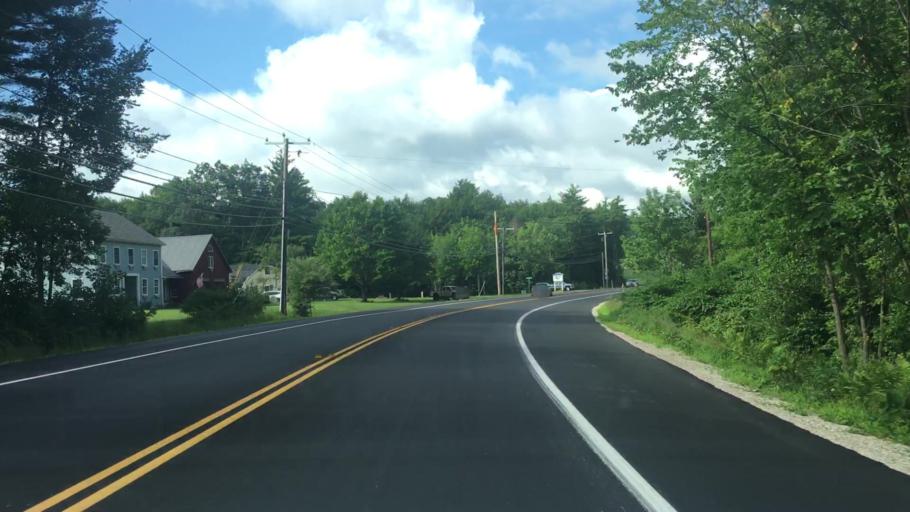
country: US
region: New Hampshire
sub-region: Belknap County
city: Gilford
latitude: 43.5460
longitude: -71.4091
